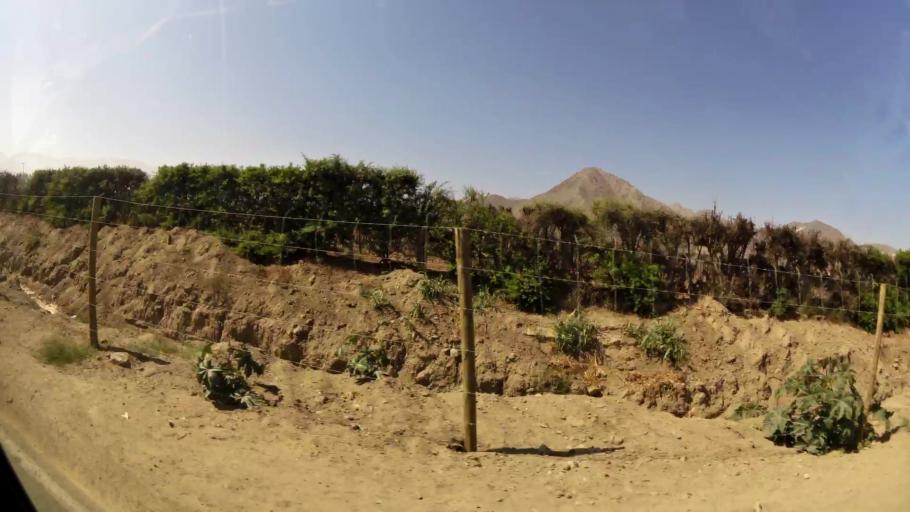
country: PE
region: Ica
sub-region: Provincia de Ica
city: San Juan Bautista
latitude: -13.9510
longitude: -75.6850
